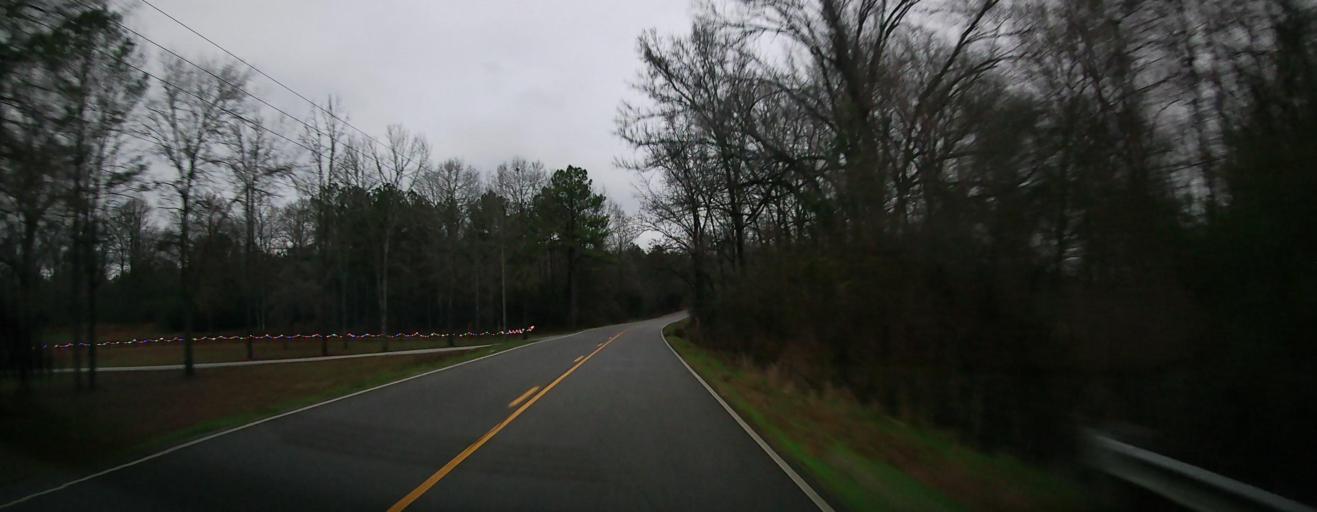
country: US
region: Alabama
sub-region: Tuscaloosa County
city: Vance
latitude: 33.1246
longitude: -87.2277
